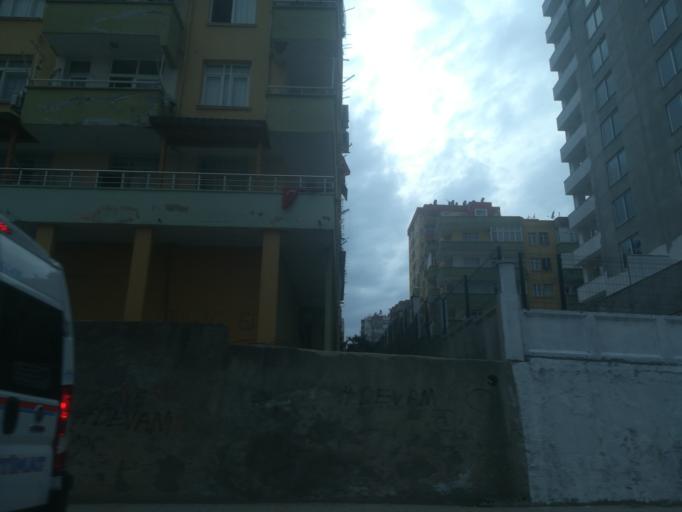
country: TR
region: Adana
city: Adana
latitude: 37.0390
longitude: 35.2931
